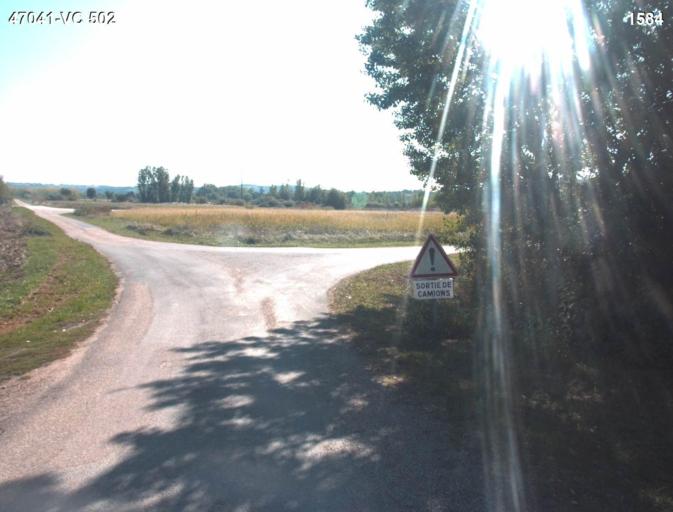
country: FR
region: Aquitaine
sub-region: Departement du Lot-et-Garonne
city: Port-Sainte-Marie
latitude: 44.2186
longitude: 0.3912
